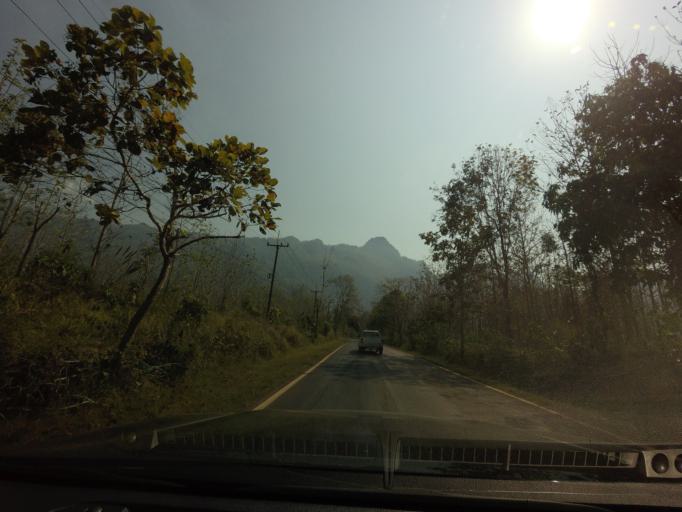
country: TH
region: Kanchanaburi
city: Thong Pha Phum
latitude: 14.6549
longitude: 98.6002
